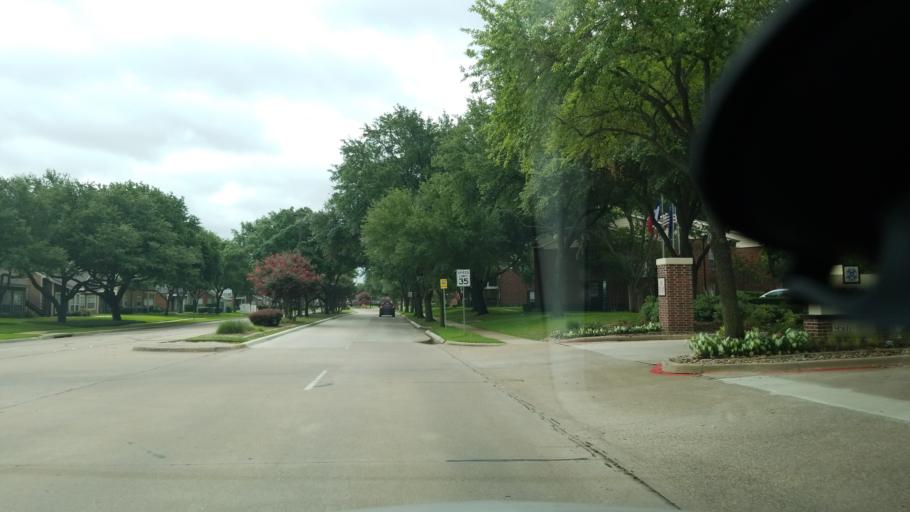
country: US
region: Texas
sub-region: Dallas County
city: Farmers Branch
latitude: 32.9375
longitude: -96.9465
